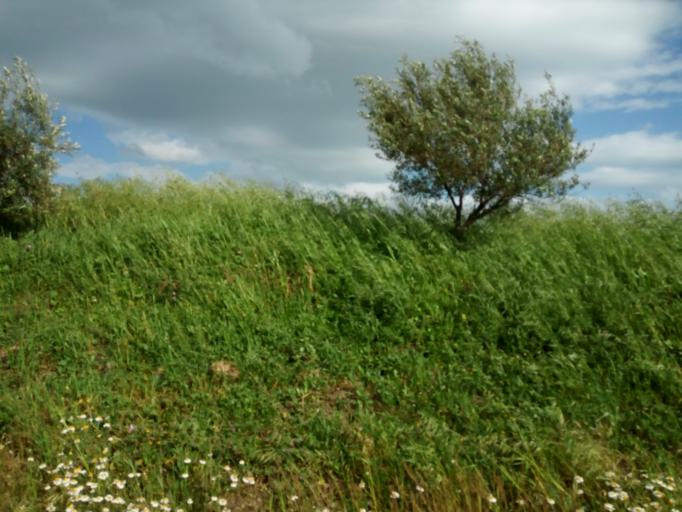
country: DZ
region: Tipaza
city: El Affroun
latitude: 36.3729
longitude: 2.5153
